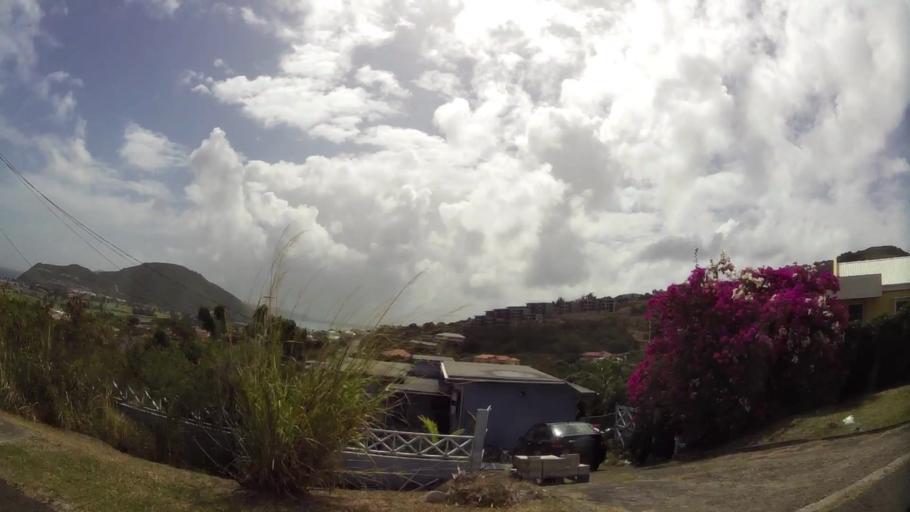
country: KN
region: Saint George Basseterre
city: Basseterre
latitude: 17.2926
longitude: -62.6944
